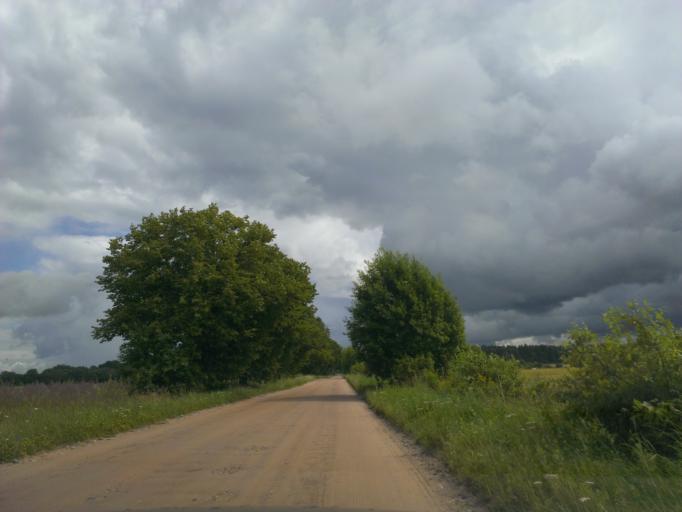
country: LV
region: Ligatne
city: Ligatne
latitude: 57.2020
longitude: 24.9758
